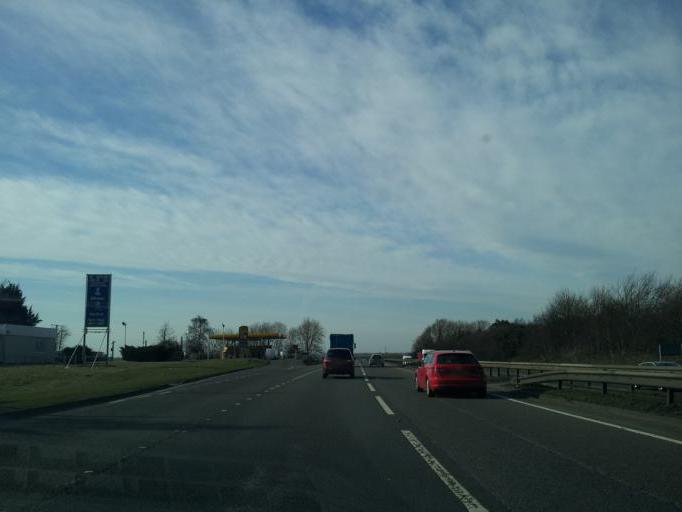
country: GB
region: England
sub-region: Lincolnshire
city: Long Bennington
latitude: 52.9719
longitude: -0.7224
